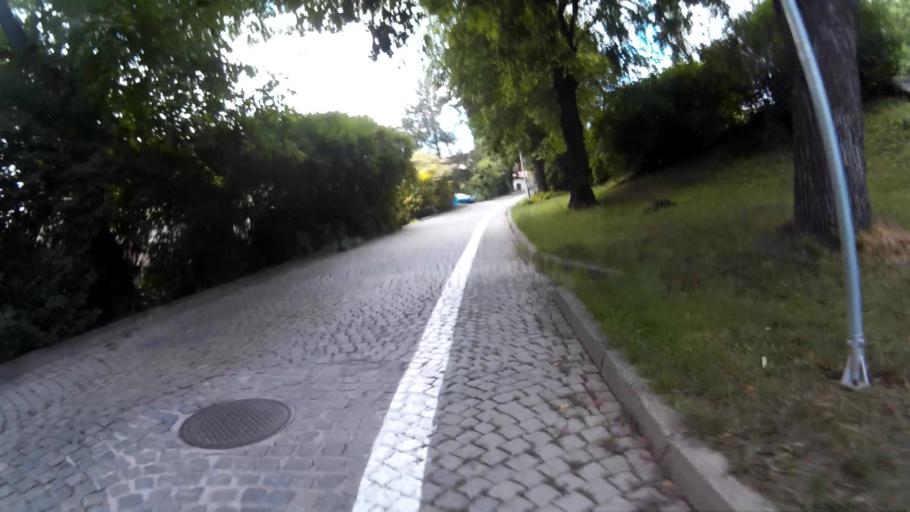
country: CZ
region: South Moravian
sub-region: Okres Brno-Venkov
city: Rosice
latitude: 49.1806
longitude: 16.3871
